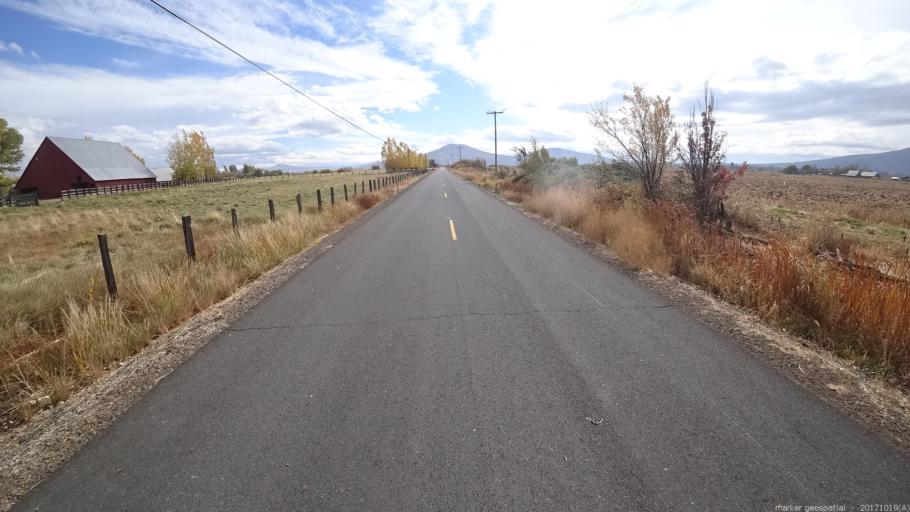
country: US
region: California
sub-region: Shasta County
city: Burney
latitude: 41.0939
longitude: -121.4932
